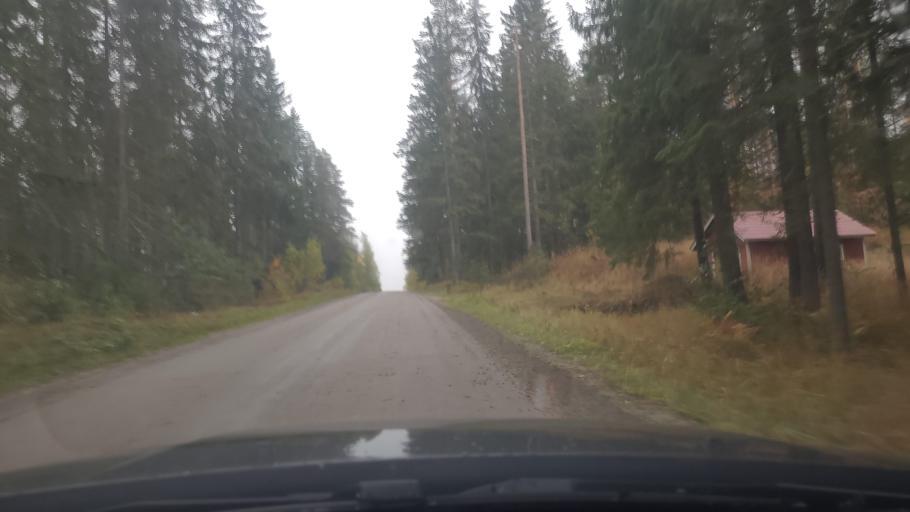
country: FI
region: Northern Savo
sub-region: Varkaus
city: Kangaslampi
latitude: 62.4491
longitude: 28.2975
